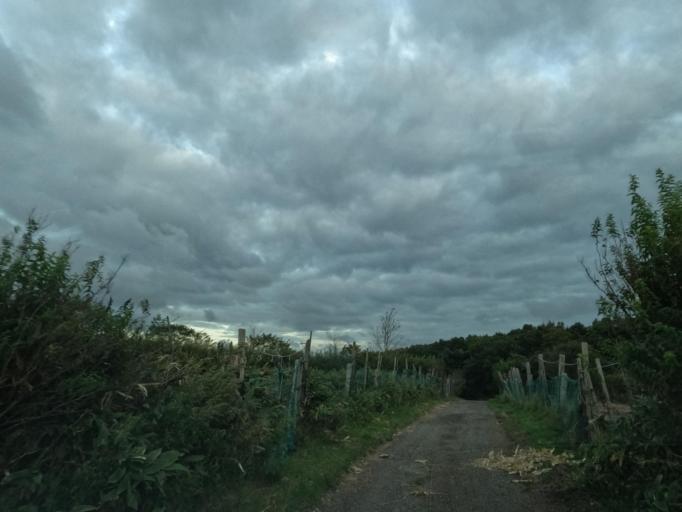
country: JP
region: Hokkaido
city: Muroran
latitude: 42.3710
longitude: 140.9710
